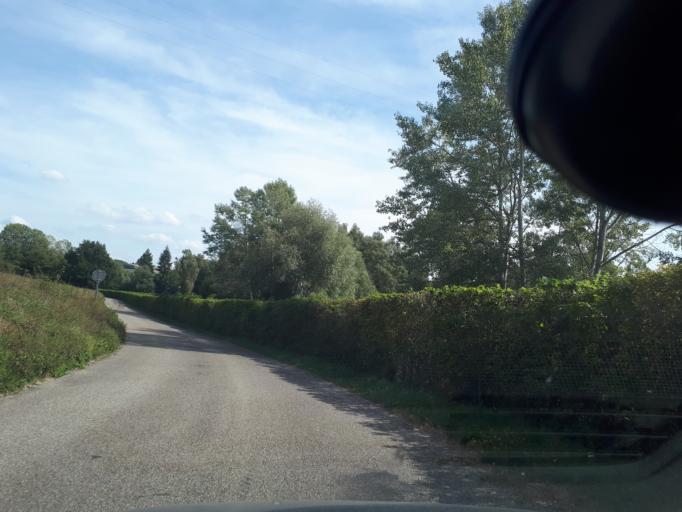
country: FR
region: Rhone-Alpes
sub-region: Departement de l'Isere
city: Chatonnay
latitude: 45.5082
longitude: 5.2071
